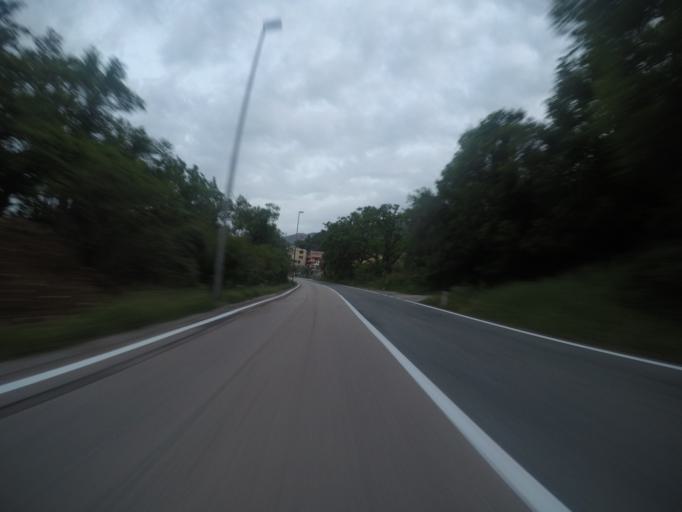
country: ME
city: Petrovac na Moru
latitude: 42.1985
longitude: 18.9683
